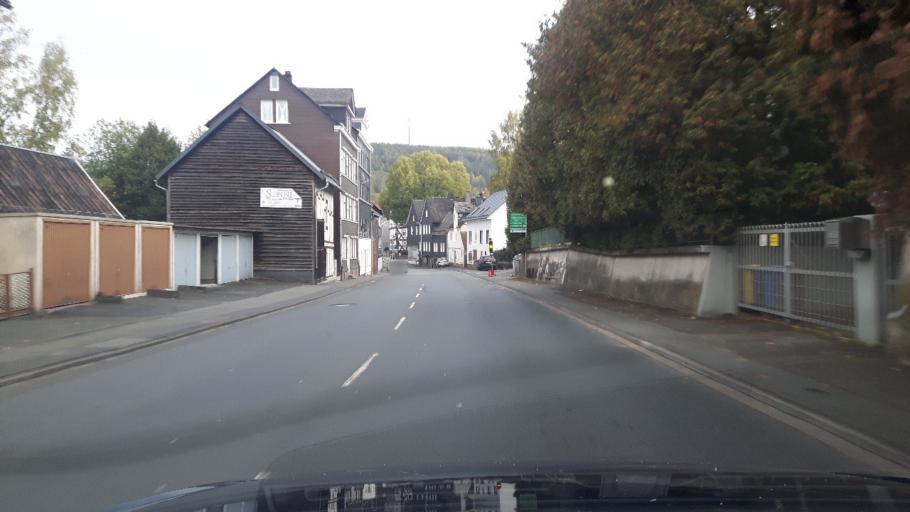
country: DE
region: North Rhine-Westphalia
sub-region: Regierungsbezirk Arnsberg
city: Bad Laasphe
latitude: 50.9286
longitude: 8.4057
